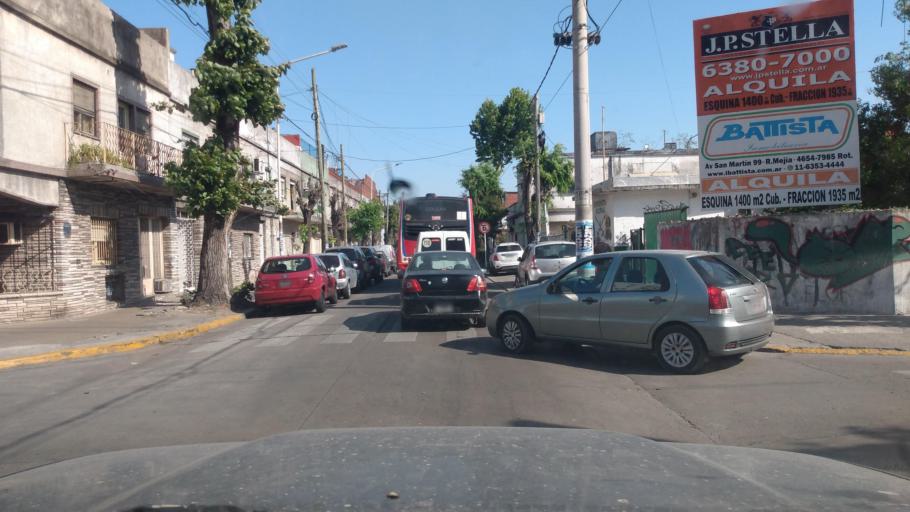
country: AR
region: Buenos Aires
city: San Justo
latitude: -34.6774
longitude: -58.5638
